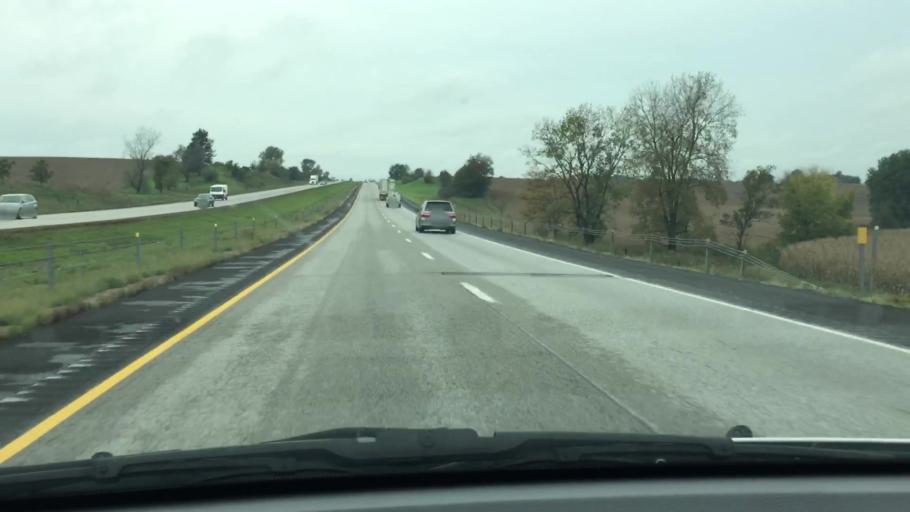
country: US
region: Iowa
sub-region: Johnson County
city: Tiffin
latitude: 41.6954
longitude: -91.7235
